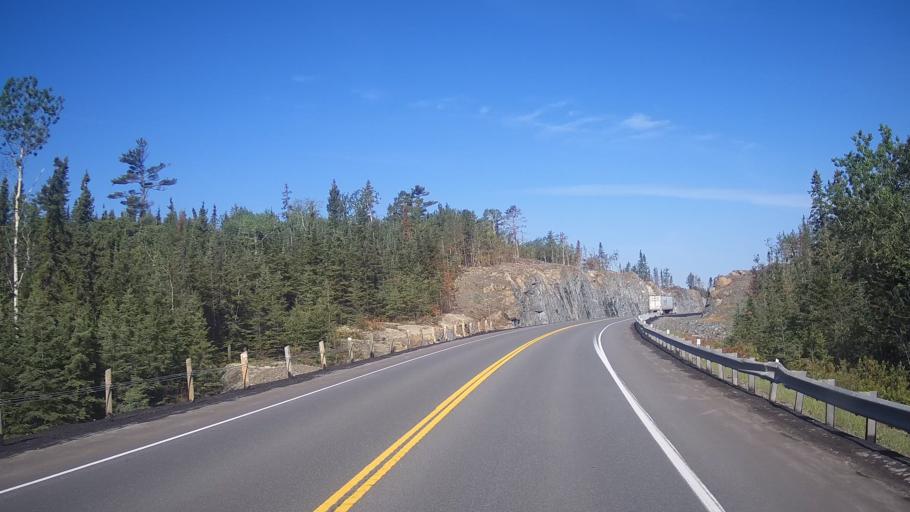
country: CA
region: Ontario
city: Dryden
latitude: 49.6477
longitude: -92.4664
